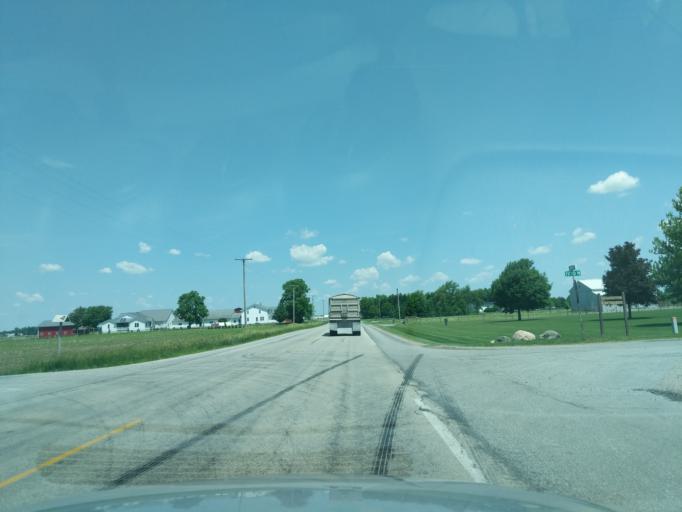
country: US
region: Indiana
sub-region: Noble County
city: Ligonier
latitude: 41.5104
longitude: -85.5778
